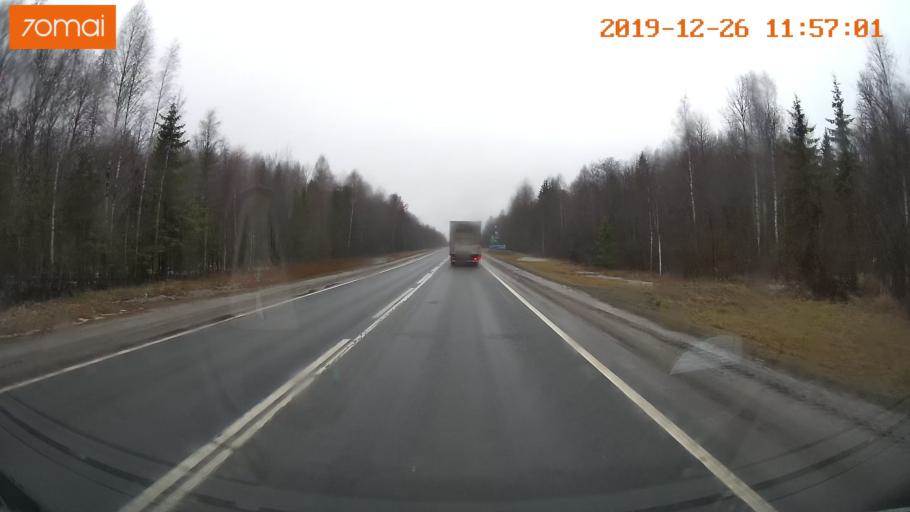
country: RU
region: Vologda
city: Sheksna
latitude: 59.2869
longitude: 38.2571
